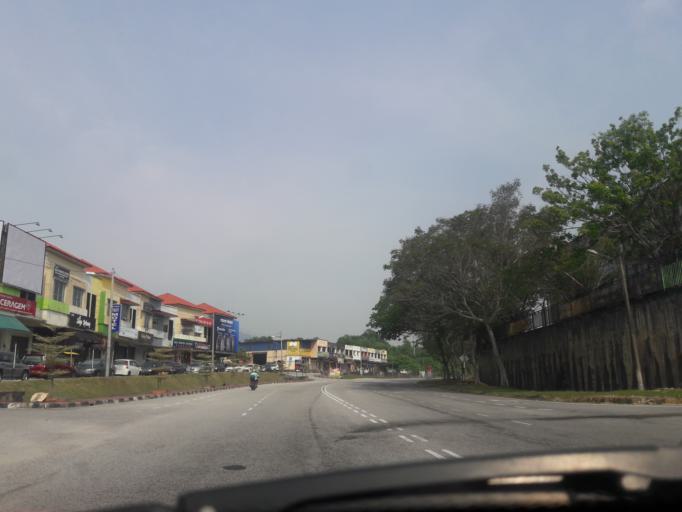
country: MY
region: Kedah
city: Kulim
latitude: 5.3668
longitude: 100.5472
